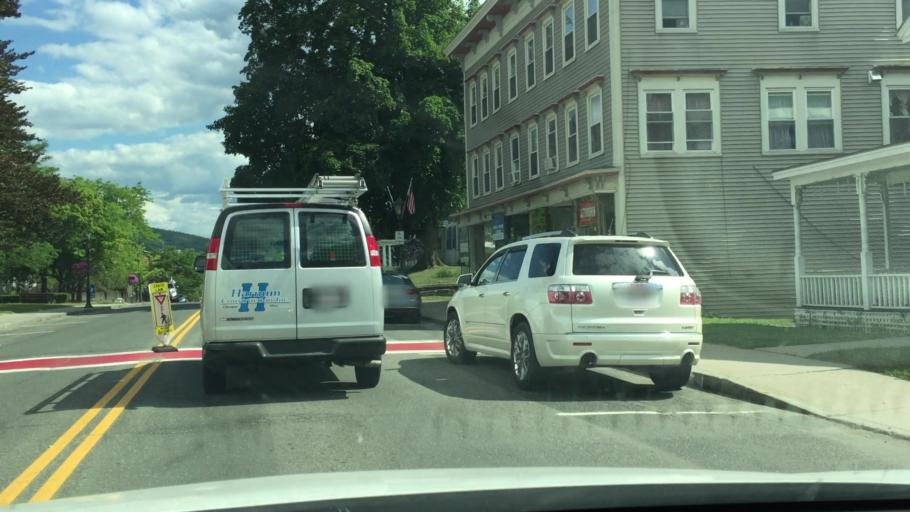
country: US
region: Massachusetts
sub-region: Berkshire County
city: Lee
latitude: 42.3072
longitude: -73.2504
